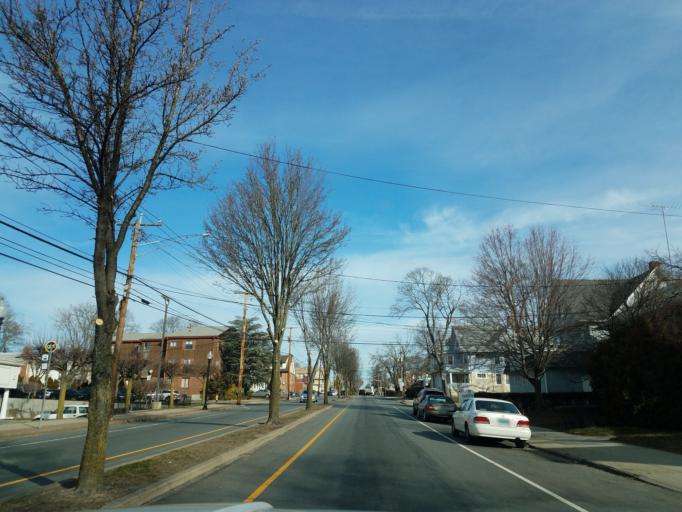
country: US
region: Connecticut
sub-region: Fairfield County
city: Bridgeport
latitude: 41.2025
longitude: -73.2040
